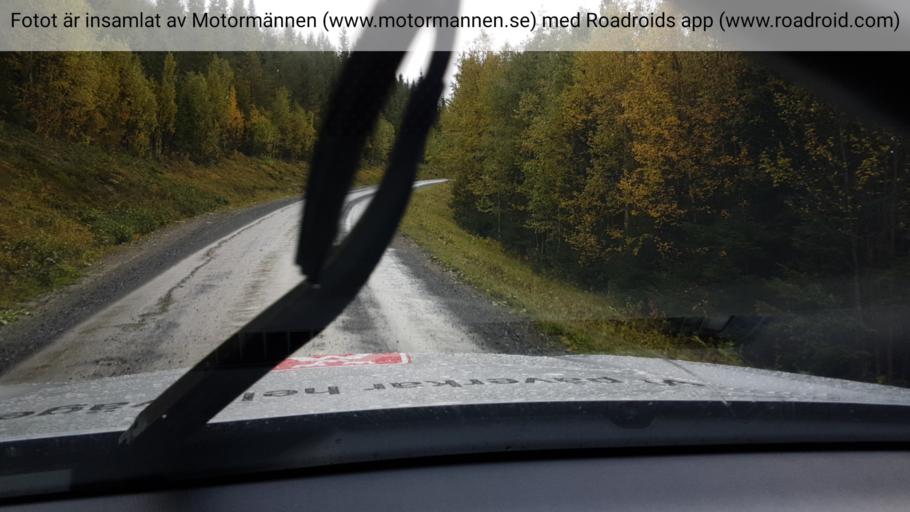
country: SE
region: Jaemtland
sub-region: Krokoms Kommun
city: Valla
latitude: 64.1077
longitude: 14.1504
